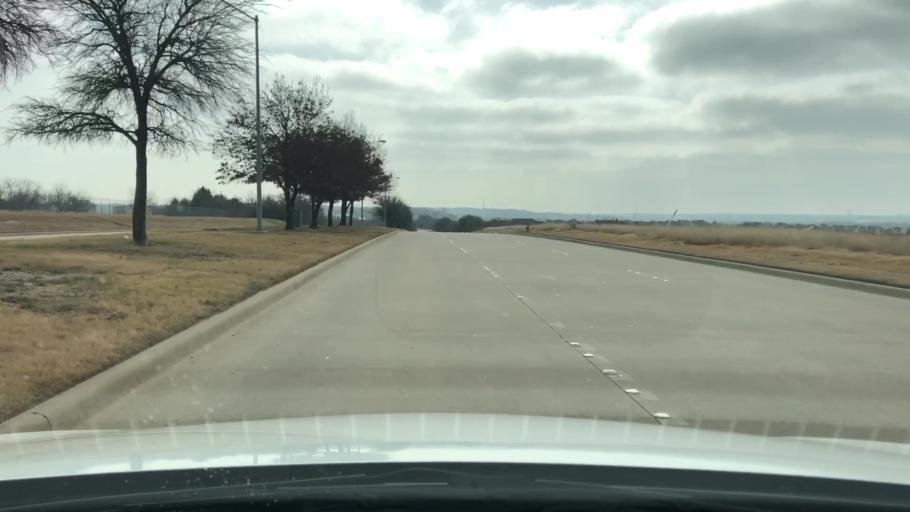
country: US
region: Texas
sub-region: Denton County
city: The Colony
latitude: 33.0786
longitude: -96.8510
